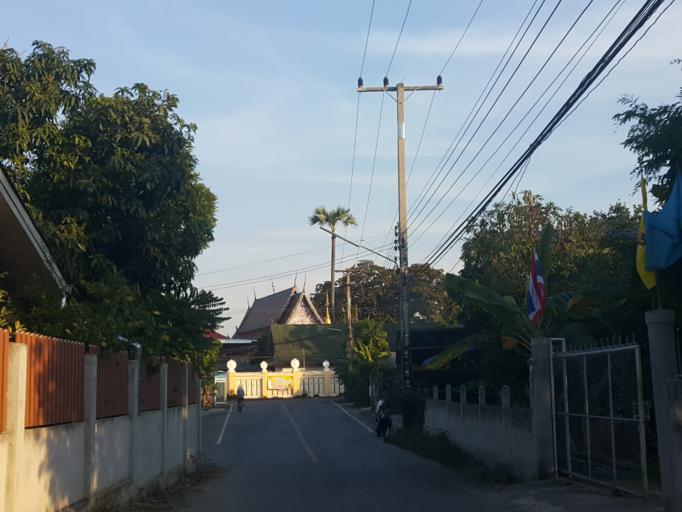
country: TH
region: Chiang Mai
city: San Sai
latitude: 18.8170
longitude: 99.0983
